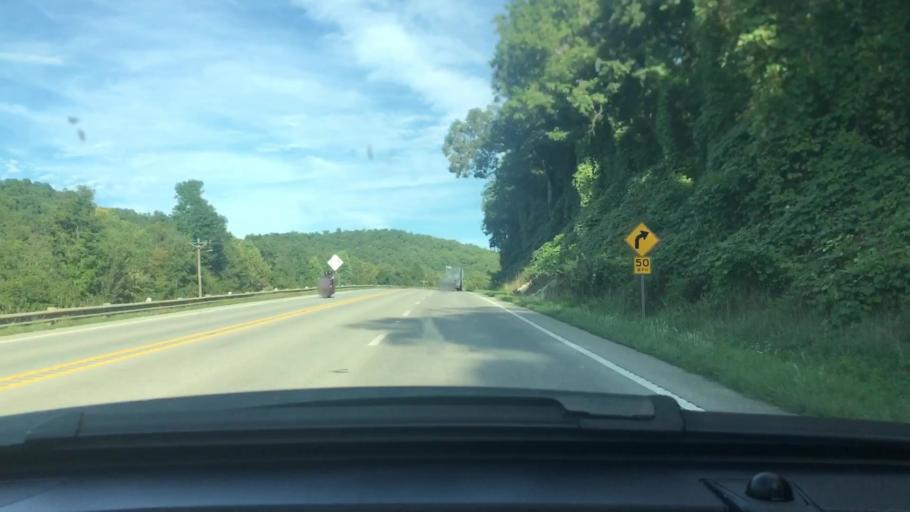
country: US
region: Arkansas
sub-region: Sharp County
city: Cherokee Village
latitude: 36.3038
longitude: -91.4198
